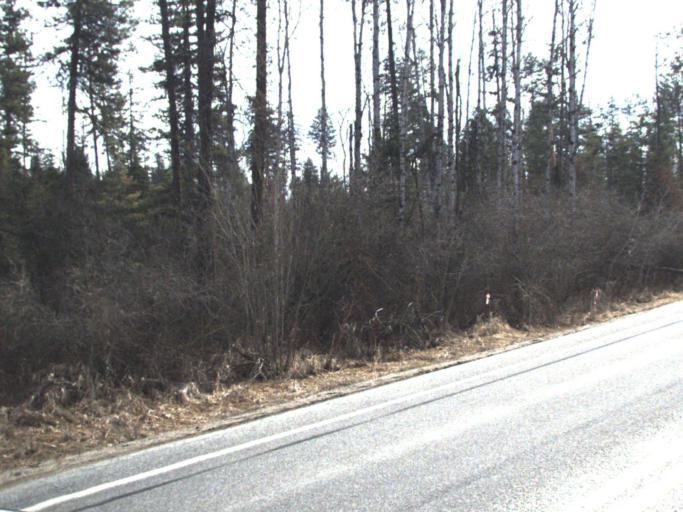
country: US
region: Washington
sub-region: Pend Oreille County
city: Newport
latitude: 48.2866
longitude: -117.2715
